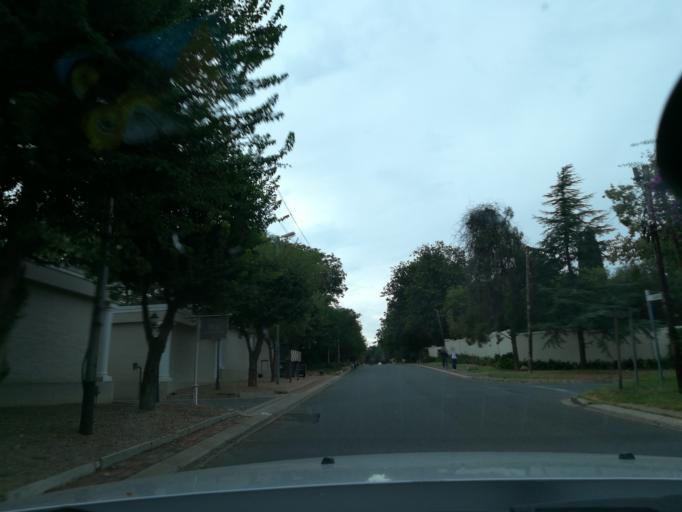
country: ZA
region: Gauteng
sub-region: City of Johannesburg Metropolitan Municipality
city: Diepsloot
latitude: -26.0681
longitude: 27.9965
